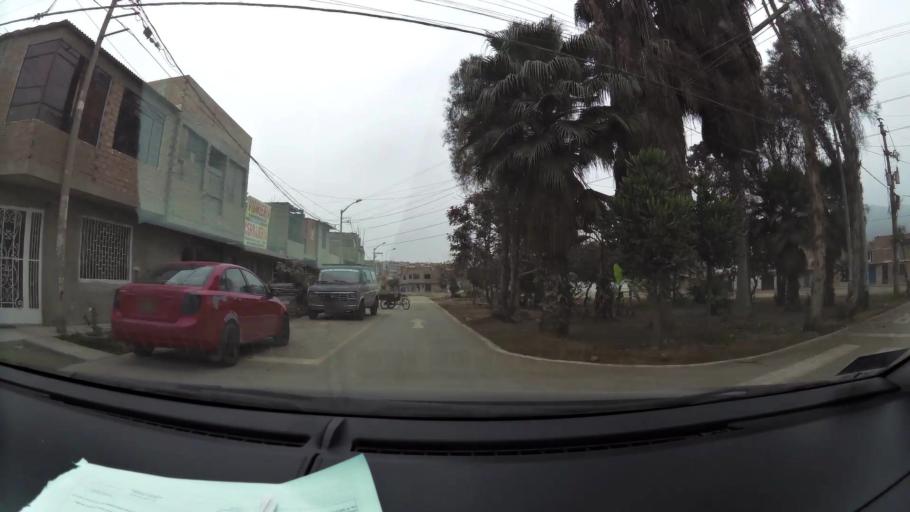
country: PE
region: Lima
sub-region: Lima
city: Urb. Santo Domingo
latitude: -11.8923
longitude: -77.0648
